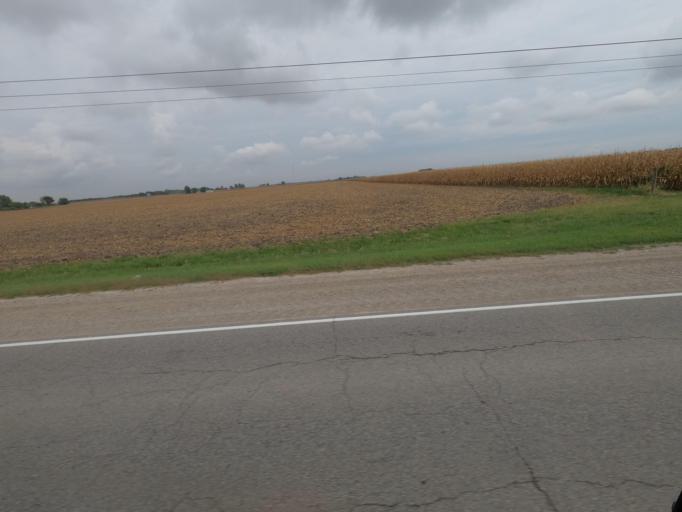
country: US
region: Iowa
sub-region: Wapello County
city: Ottumwa
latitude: 40.9467
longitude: -92.2272
